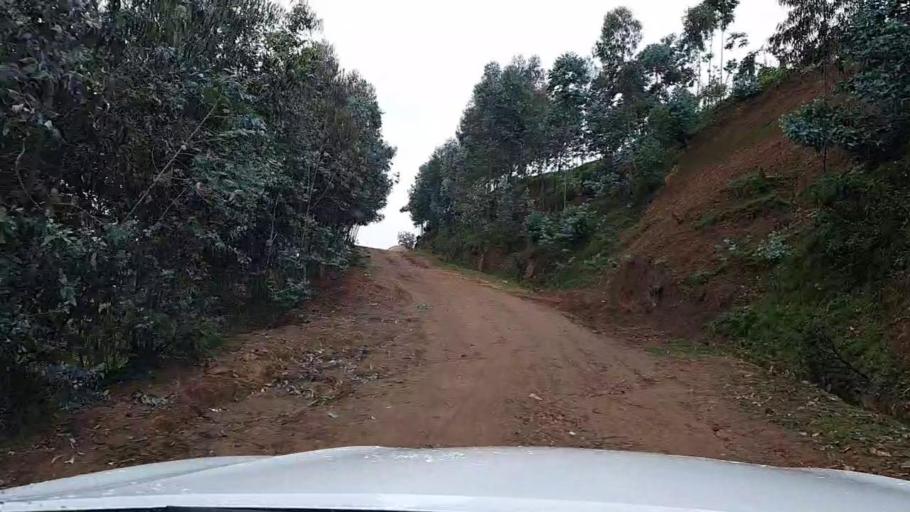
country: RW
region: Southern Province
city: Nzega
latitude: -2.4557
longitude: 29.4709
